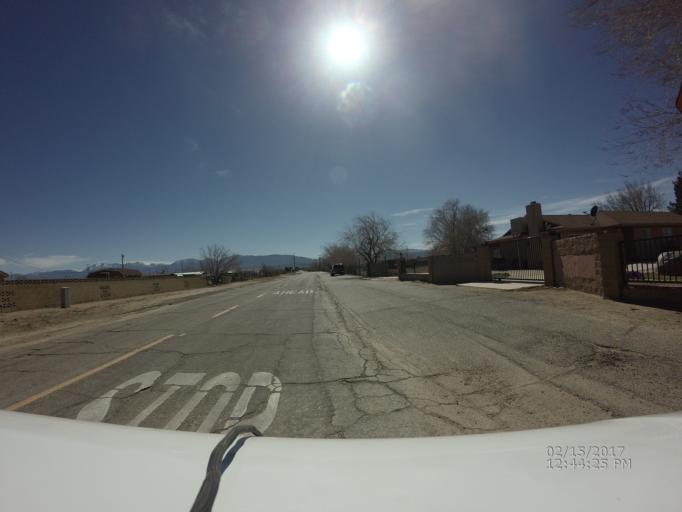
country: US
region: California
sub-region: Los Angeles County
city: Littlerock
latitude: 34.5741
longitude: -117.9610
